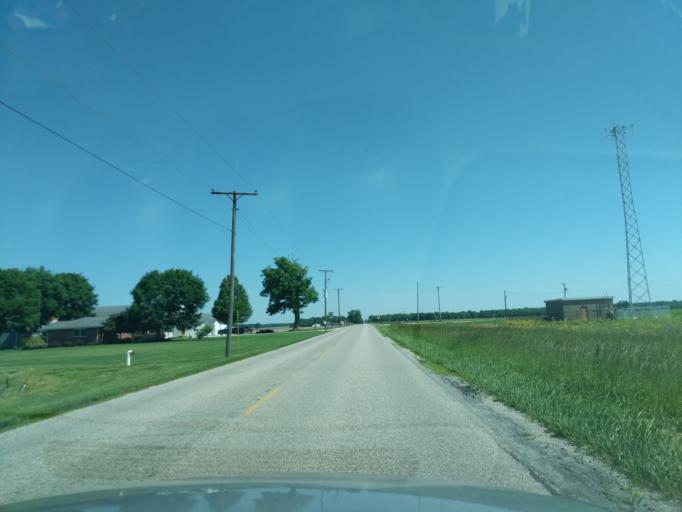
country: US
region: Indiana
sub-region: Huntington County
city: Warren
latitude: 40.7622
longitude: -85.5072
